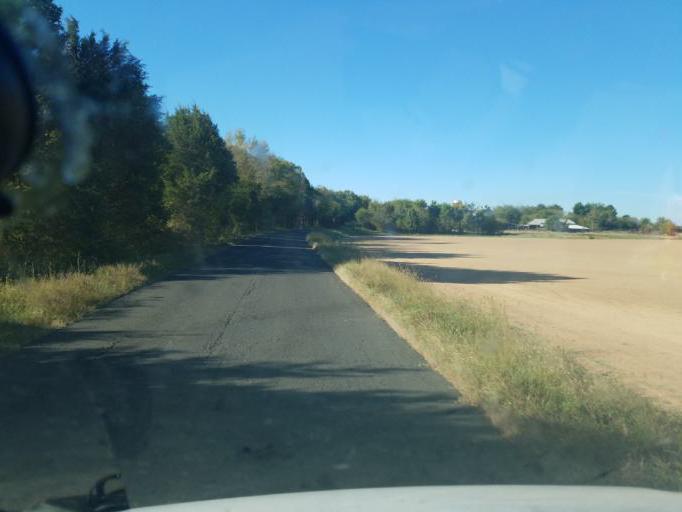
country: US
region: Virginia
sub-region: Fauquier County
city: Bealeton
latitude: 38.5390
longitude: -77.8147
